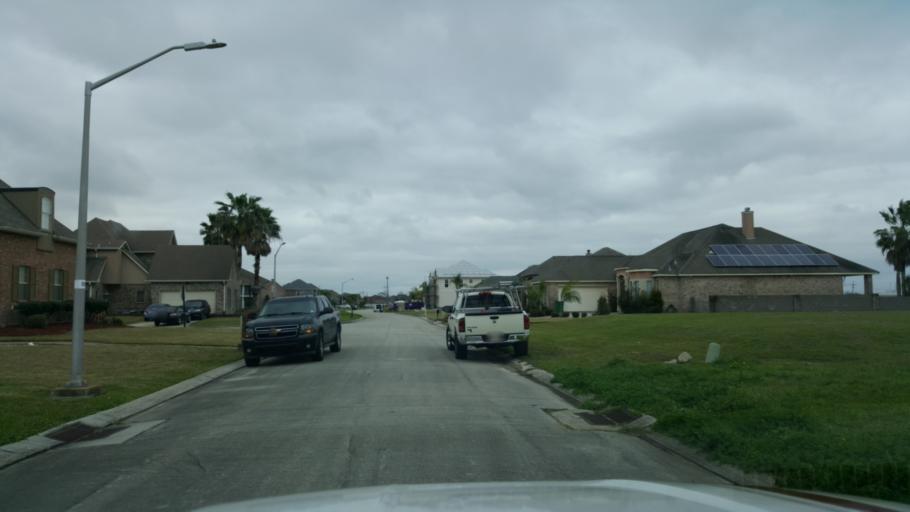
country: US
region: Louisiana
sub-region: Jefferson Parish
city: Woodmere
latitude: 29.8721
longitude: -90.0752
